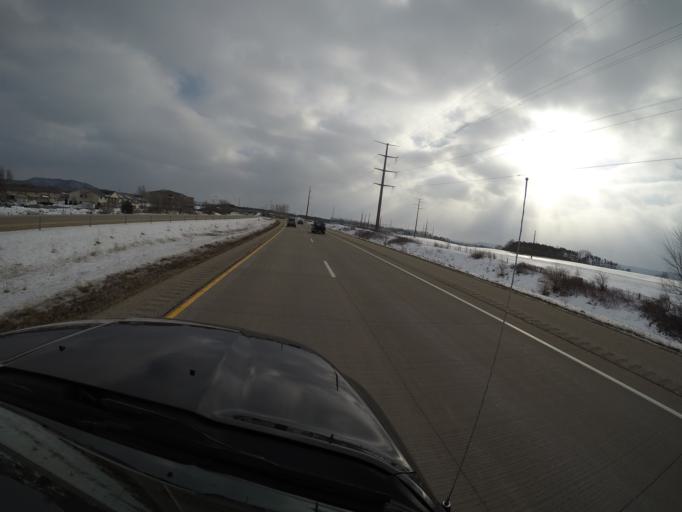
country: US
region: Wisconsin
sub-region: La Crosse County
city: Brice Prairie
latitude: 43.9588
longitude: -91.2843
